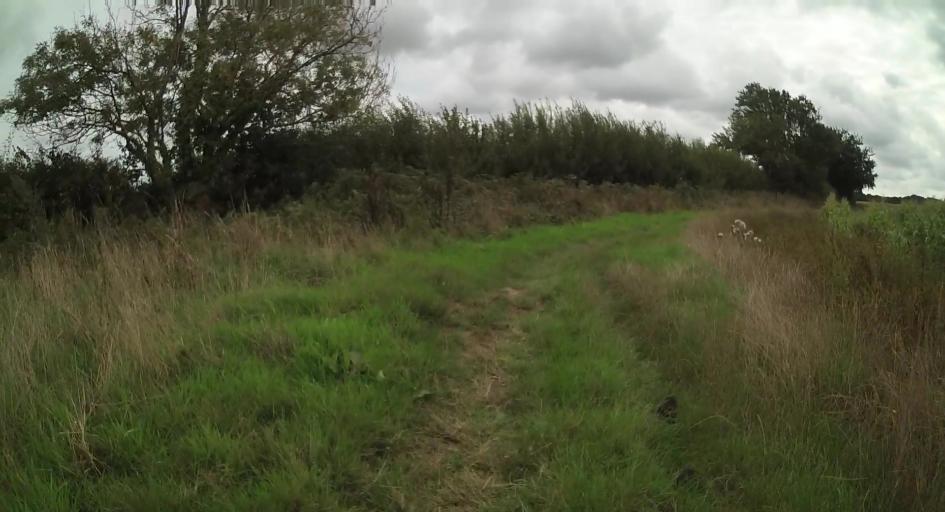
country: GB
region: England
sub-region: Isle of Wight
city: Newport
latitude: 50.6616
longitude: -1.2647
